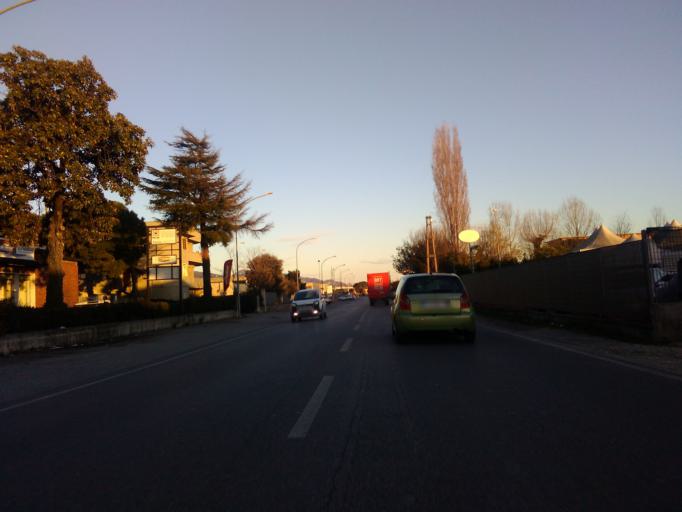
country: IT
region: Tuscany
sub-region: Provincia di Massa-Carrara
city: Carrara
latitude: 44.0356
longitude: 10.0808
